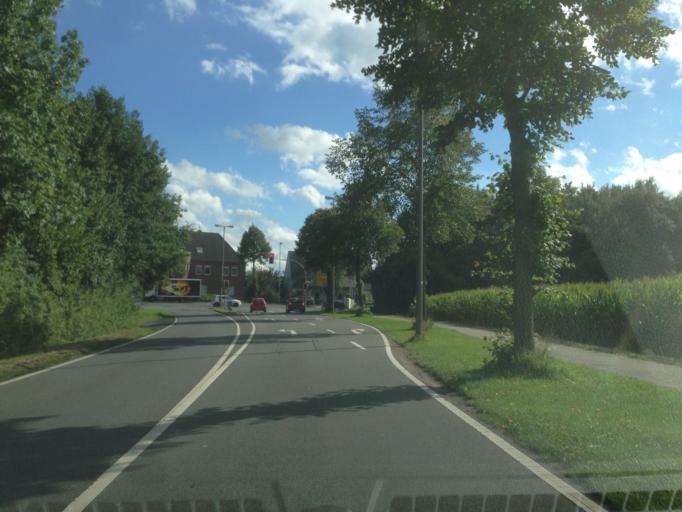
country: DE
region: North Rhine-Westphalia
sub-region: Regierungsbezirk Munster
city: Muenster
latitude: 51.9295
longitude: 7.5890
